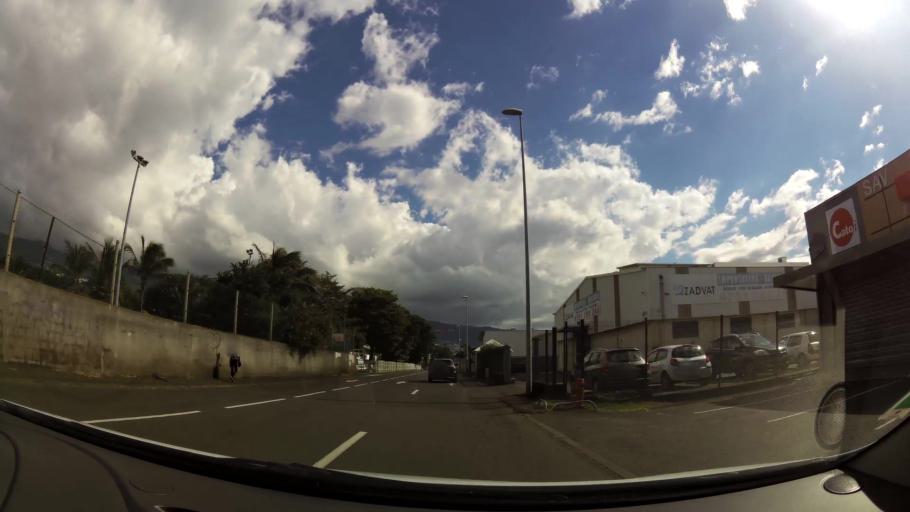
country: RE
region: Reunion
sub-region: Reunion
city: Saint-Denis
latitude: -20.8921
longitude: 55.4944
